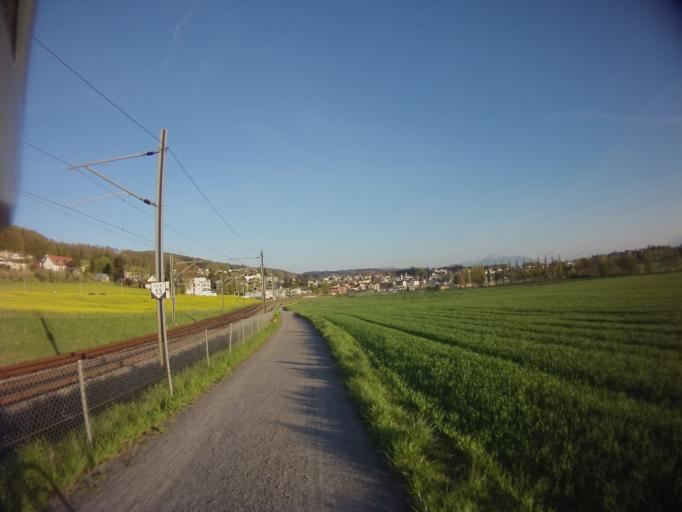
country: CH
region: Zurich
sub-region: Bezirk Affoltern
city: Hedingen
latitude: 47.2910
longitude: 8.4486
